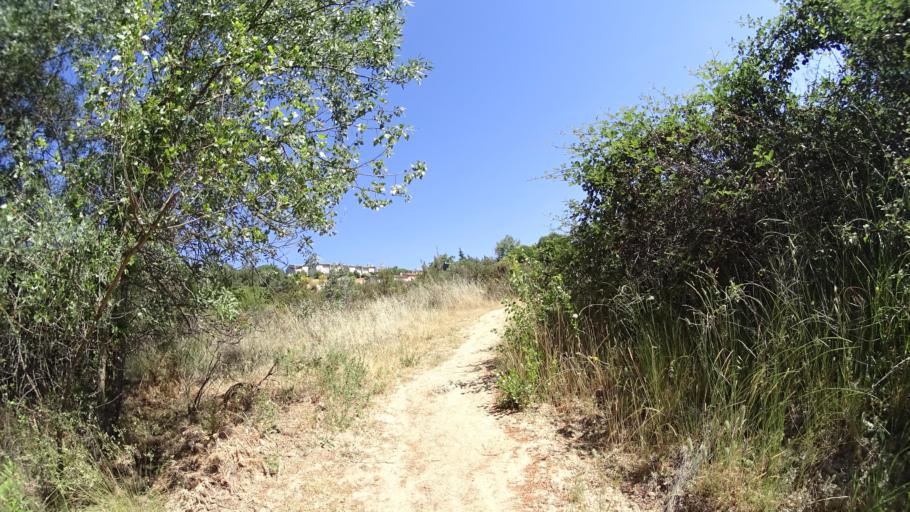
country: ES
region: Madrid
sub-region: Provincia de Madrid
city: Torrelodones
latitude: 40.5922
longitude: -3.9605
